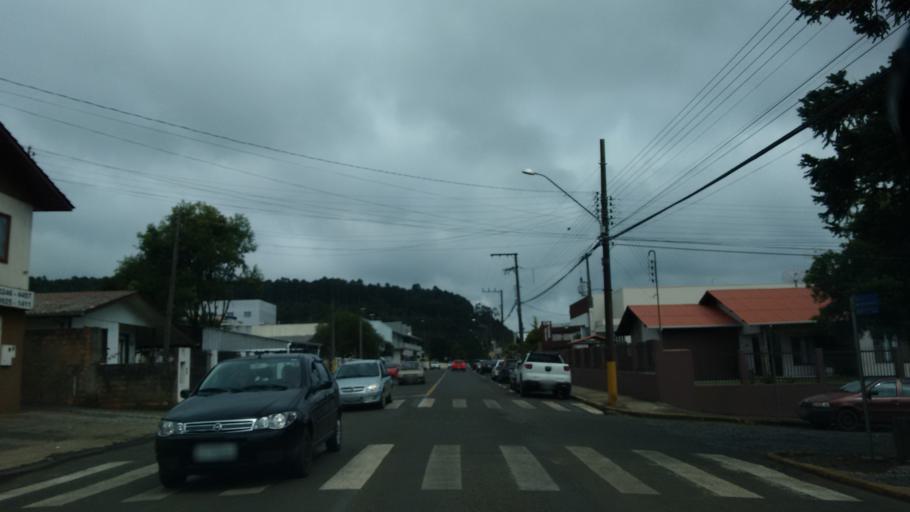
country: BR
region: Santa Catarina
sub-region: Videira
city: Videira
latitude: -27.0209
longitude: -50.9310
